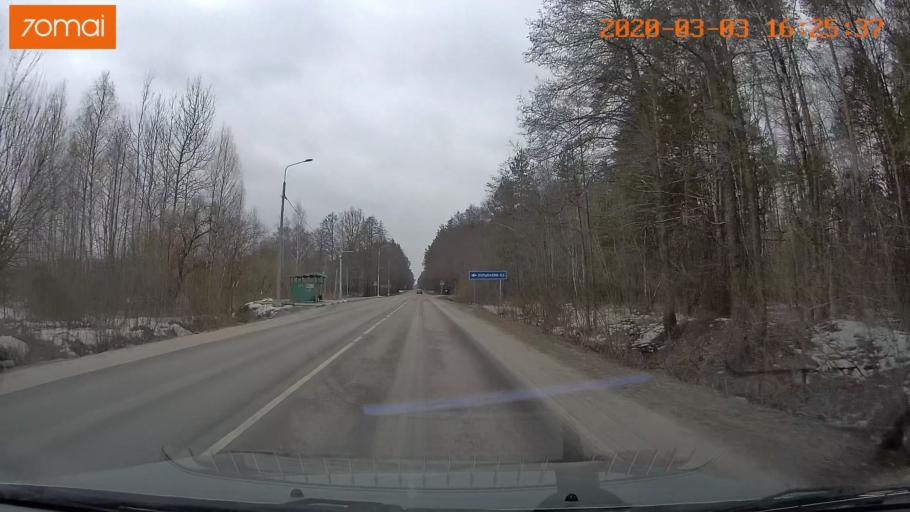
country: RU
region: Moskovskaya
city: Konobeyevo
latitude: 55.4494
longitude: 38.6594
